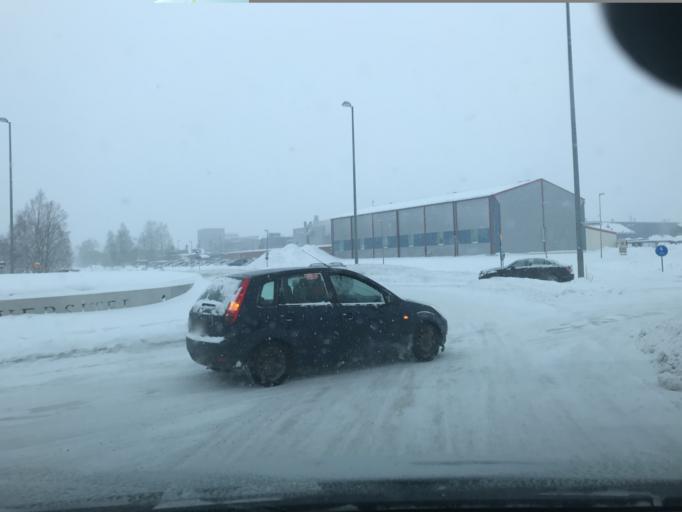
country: SE
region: Norrbotten
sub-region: Lulea Kommun
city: Lulea
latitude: 65.6156
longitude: 22.1321
